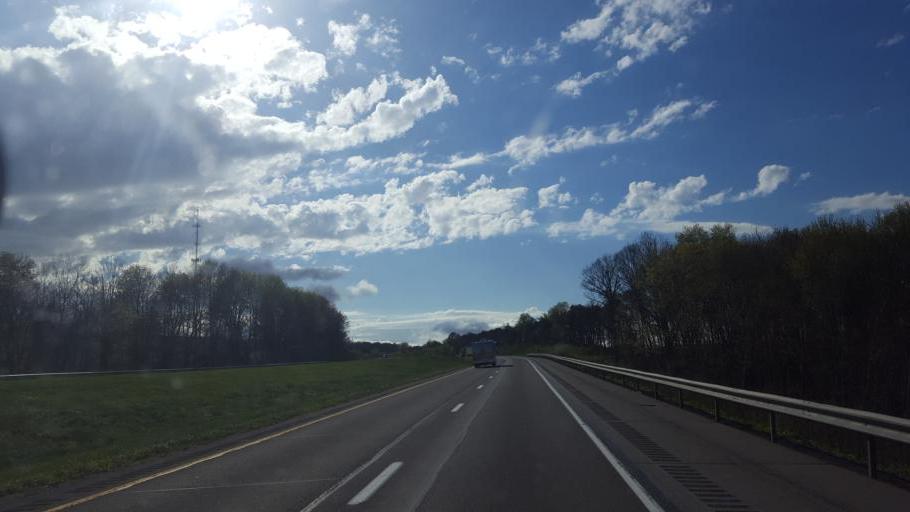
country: US
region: Pennsylvania
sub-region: Venango County
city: Franklin
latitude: 41.1957
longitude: -79.8129
